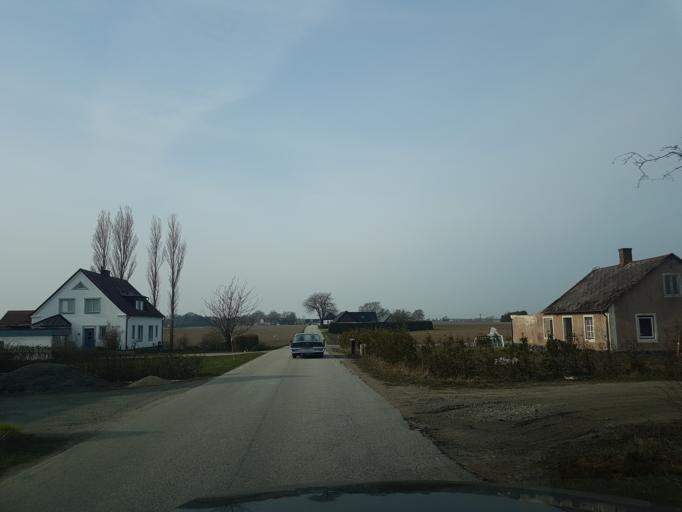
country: SE
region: Skane
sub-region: Ystads Kommun
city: Ystad
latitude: 55.4586
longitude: 13.8271
